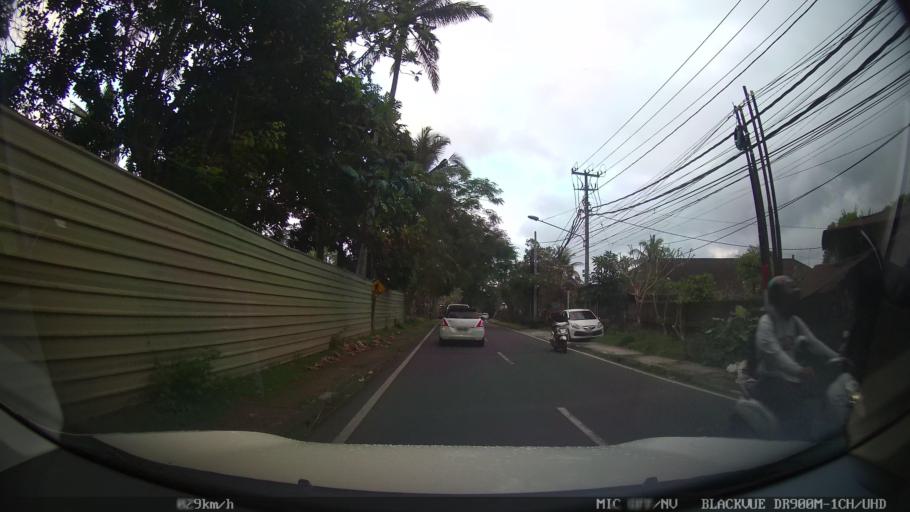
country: ID
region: Bali
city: Bunutan
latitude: -8.4699
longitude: 115.2494
